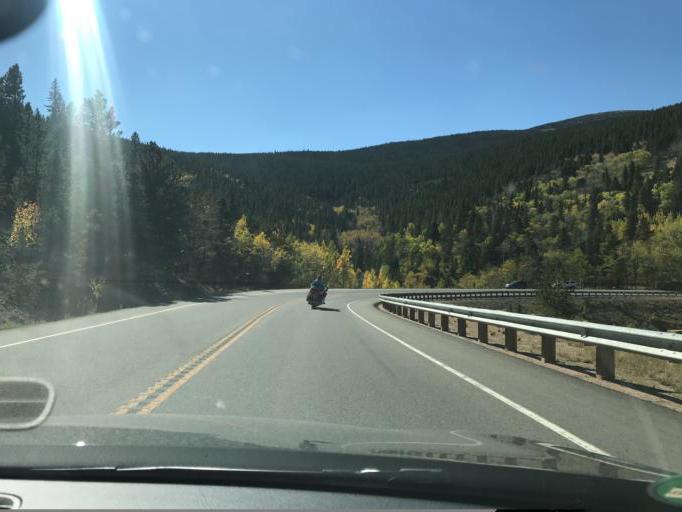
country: US
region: Colorado
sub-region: Boulder County
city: Nederland
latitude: 40.0535
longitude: -105.5235
